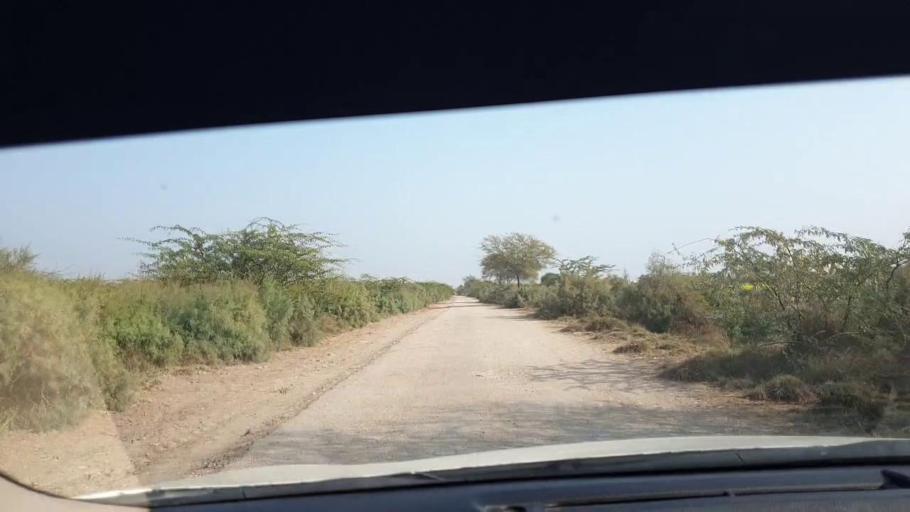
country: PK
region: Sindh
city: Berani
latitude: 25.8237
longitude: 68.7625
